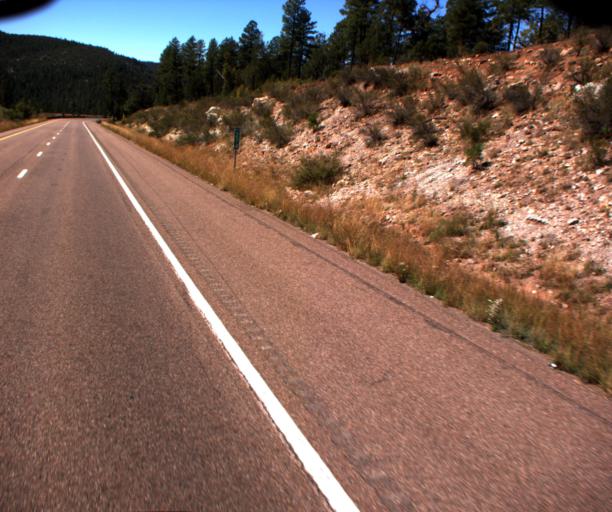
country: US
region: Arizona
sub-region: Gila County
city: Star Valley
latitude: 34.3101
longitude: -111.0160
